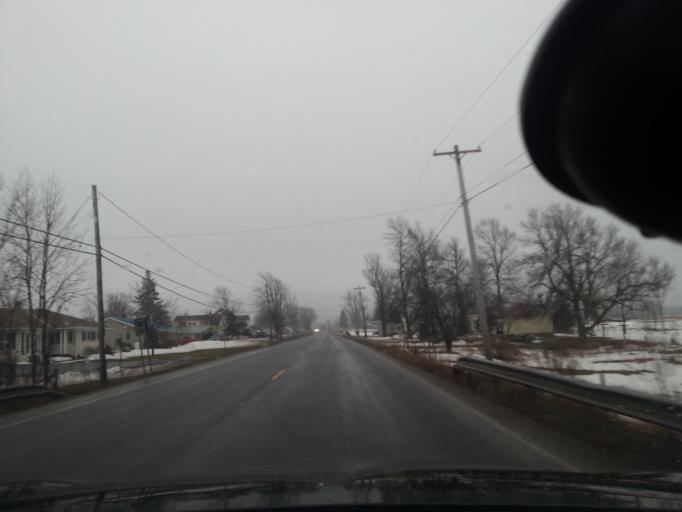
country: US
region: New York
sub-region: St. Lawrence County
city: Ogdensburg
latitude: 44.6710
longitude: -75.4719
